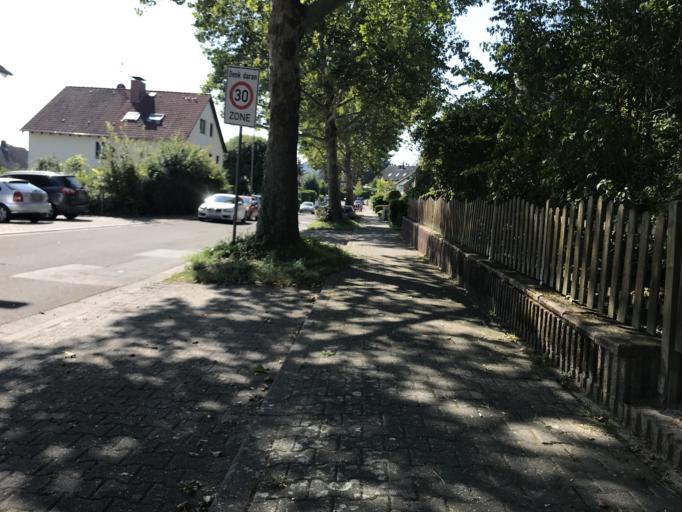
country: DE
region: Rheinland-Pfalz
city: Bodenheim
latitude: 49.9559
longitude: 8.3087
